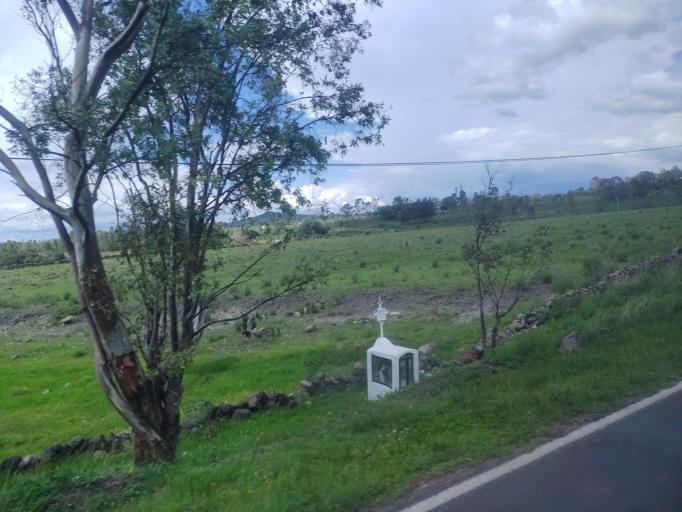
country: MX
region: Mexico
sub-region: Aculco
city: El Colorado
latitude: 20.0918
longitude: -99.7808
